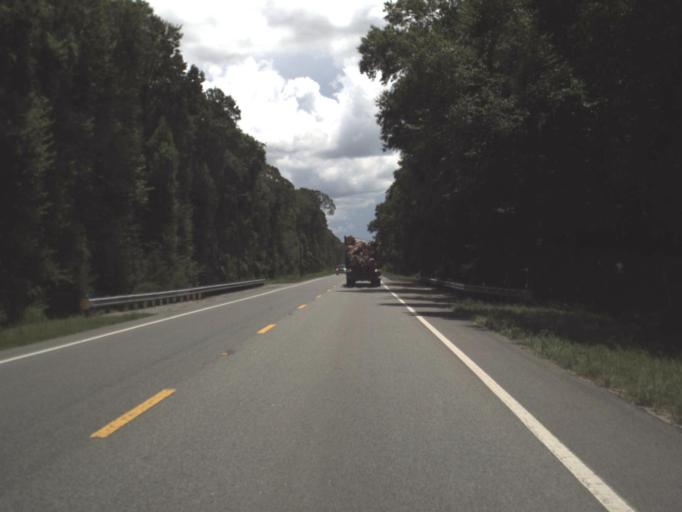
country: US
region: Florida
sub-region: Taylor County
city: Perry
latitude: 30.1218
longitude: -83.7348
